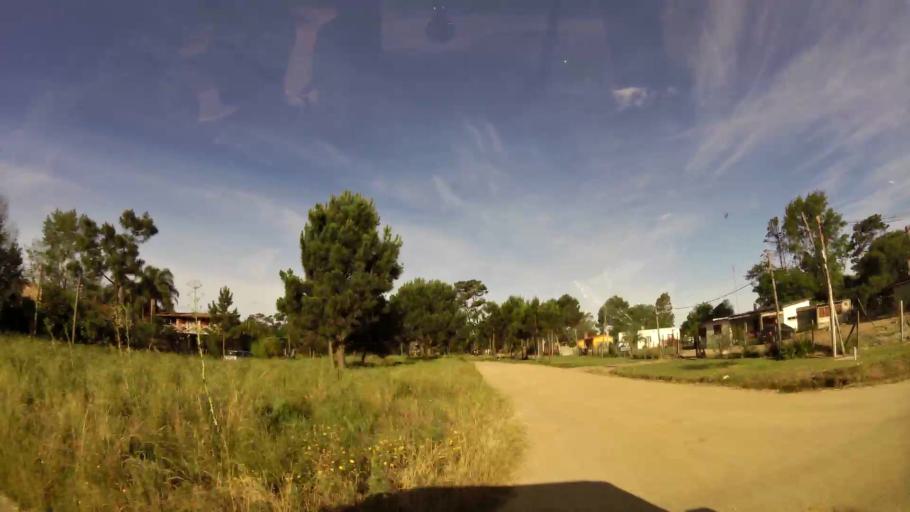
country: UY
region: Canelones
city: Empalme Olmos
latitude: -34.7756
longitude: -55.8561
